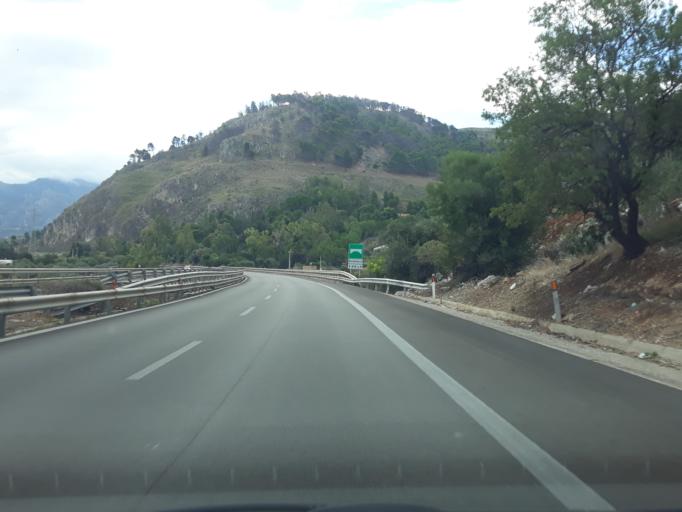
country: IT
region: Sicily
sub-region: Palermo
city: Trabia
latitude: 37.9874
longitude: 13.6557
